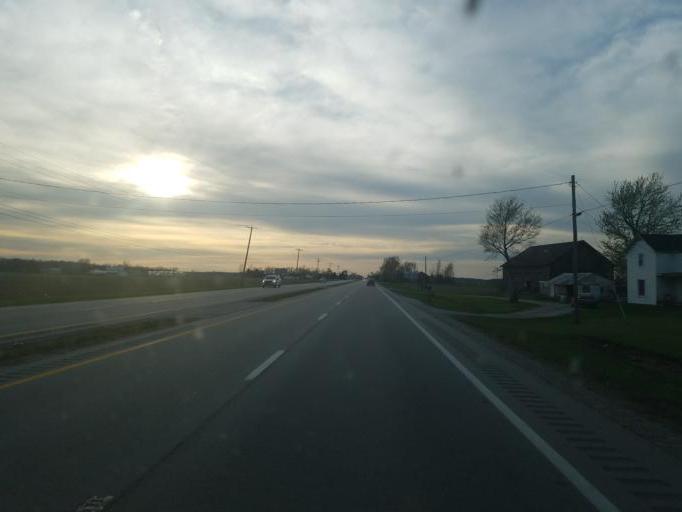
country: US
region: Ohio
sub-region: Sandusky County
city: Gibsonburg
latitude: 41.4134
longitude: -83.2713
